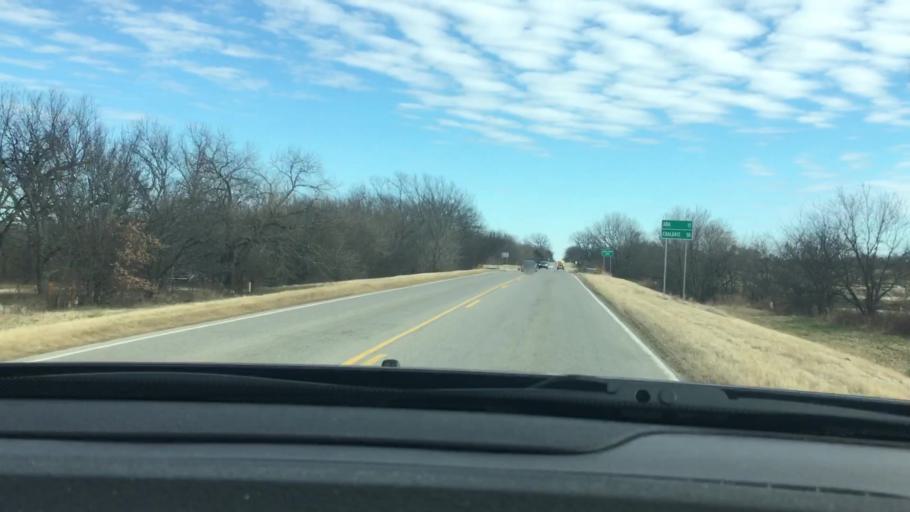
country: US
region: Oklahoma
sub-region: Garvin County
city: Stratford
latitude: 34.7966
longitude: -96.9463
